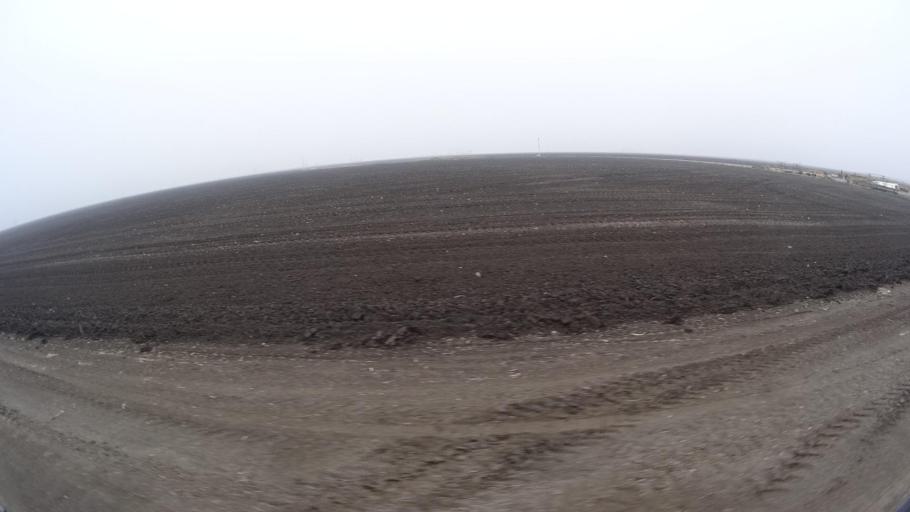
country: US
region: California
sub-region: Kern County
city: Buttonwillow
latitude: 35.4124
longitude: -119.5028
